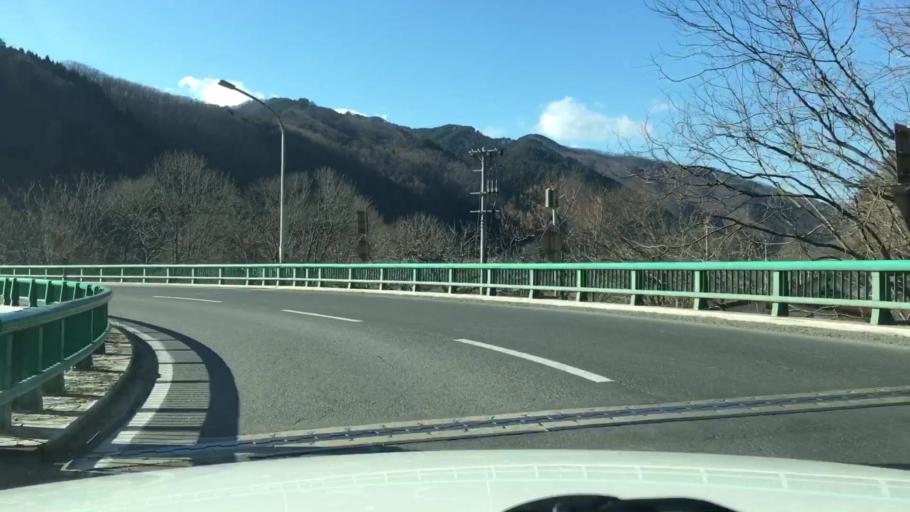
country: JP
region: Iwate
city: Miyako
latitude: 39.6207
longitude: 141.8034
